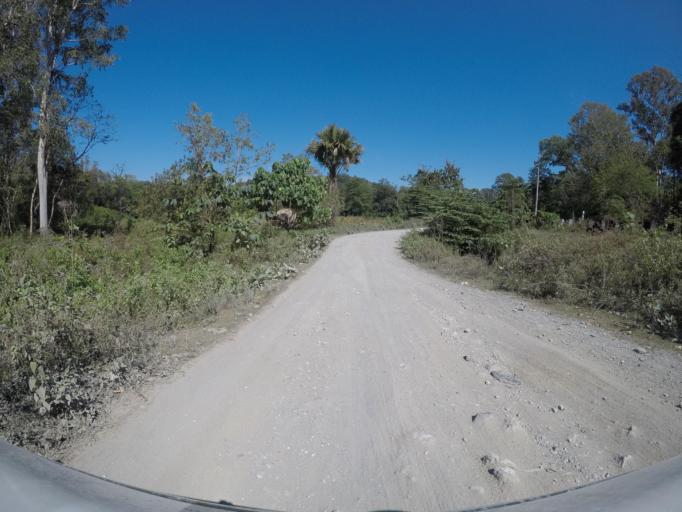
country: TL
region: Manufahi
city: Same
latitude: -8.9596
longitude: 126.0104
